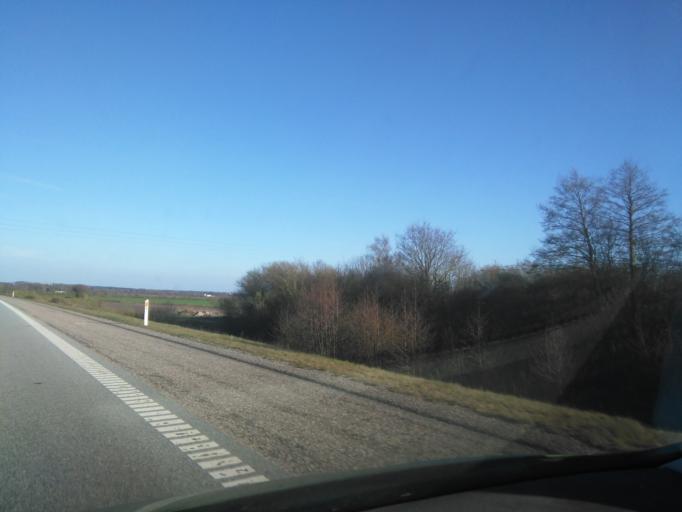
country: DK
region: Central Jutland
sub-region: Herning Kommune
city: Snejbjerg
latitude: 56.1167
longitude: 8.9142
